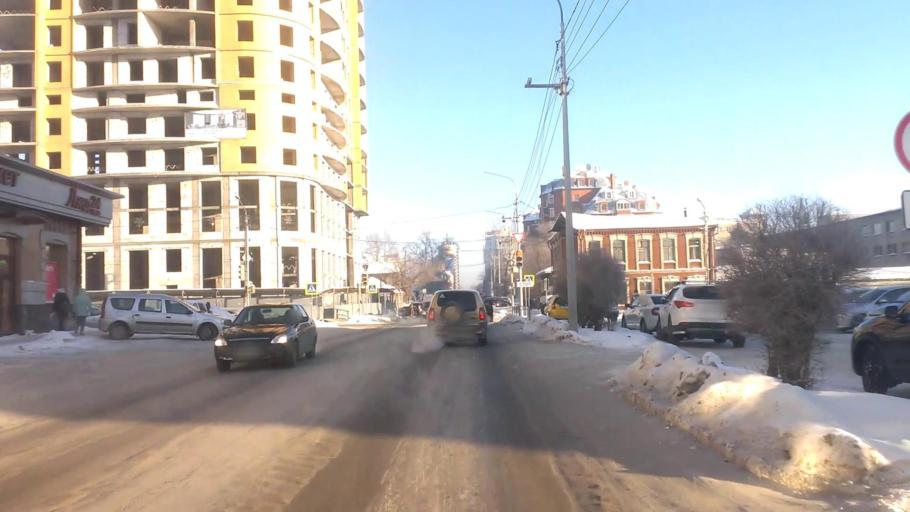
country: RU
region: Altai Krai
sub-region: Gorod Barnaulskiy
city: Barnaul
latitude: 53.3380
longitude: 83.7809
